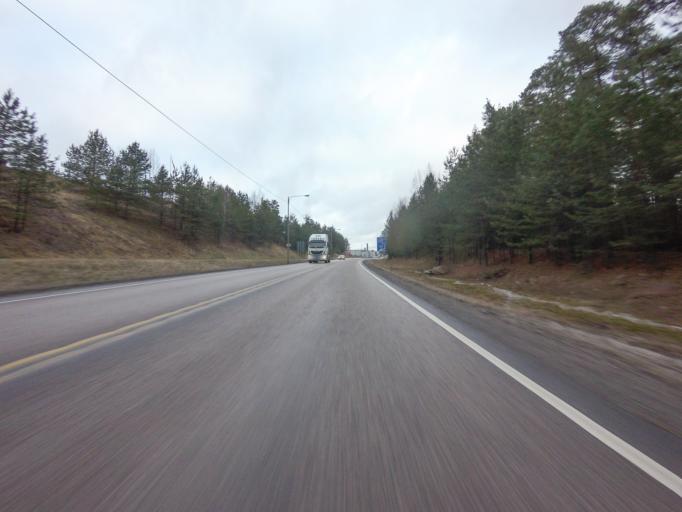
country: FI
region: Uusimaa
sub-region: Helsinki
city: Lohja
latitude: 60.2208
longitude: 24.0266
